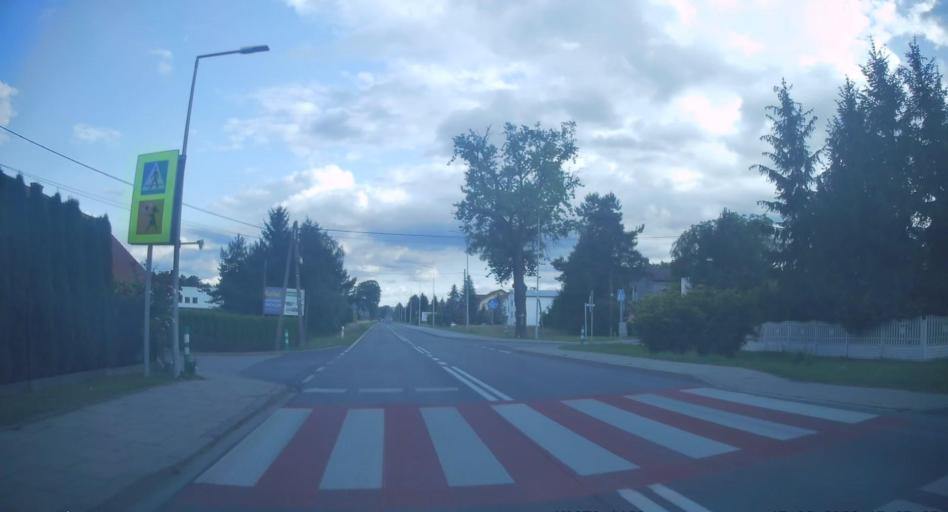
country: PL
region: Lesser Poland Voivodeship
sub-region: Powiat oswiecimski
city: Nowa Wies
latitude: 49.9491
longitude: 19.2093
